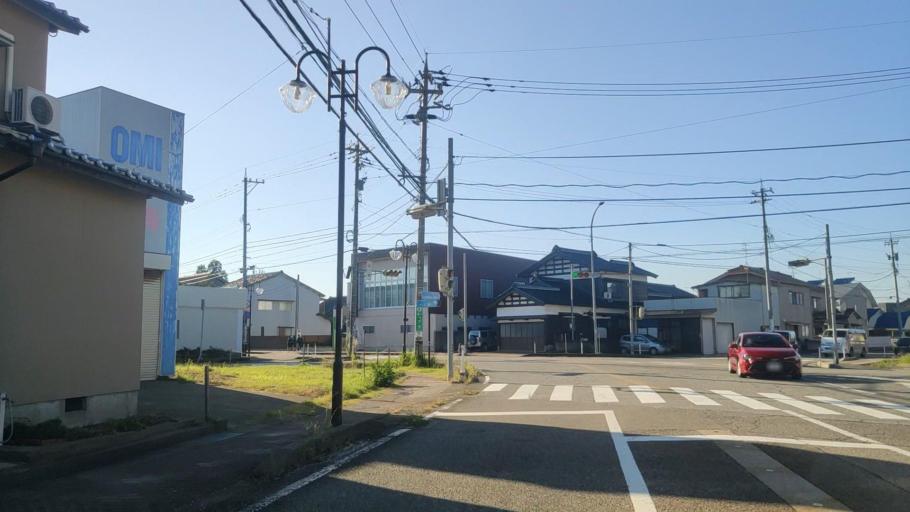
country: JP
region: Ishikawa
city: Tsubata
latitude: 36.6730
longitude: 136.7311
